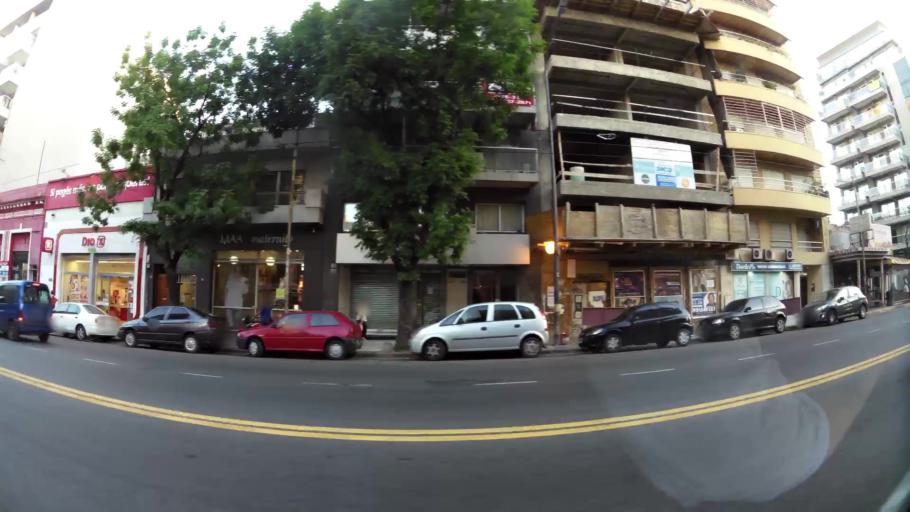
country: AR
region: Buenos Aires F.D.
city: Colegiales
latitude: -34.5906
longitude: -58.4247
